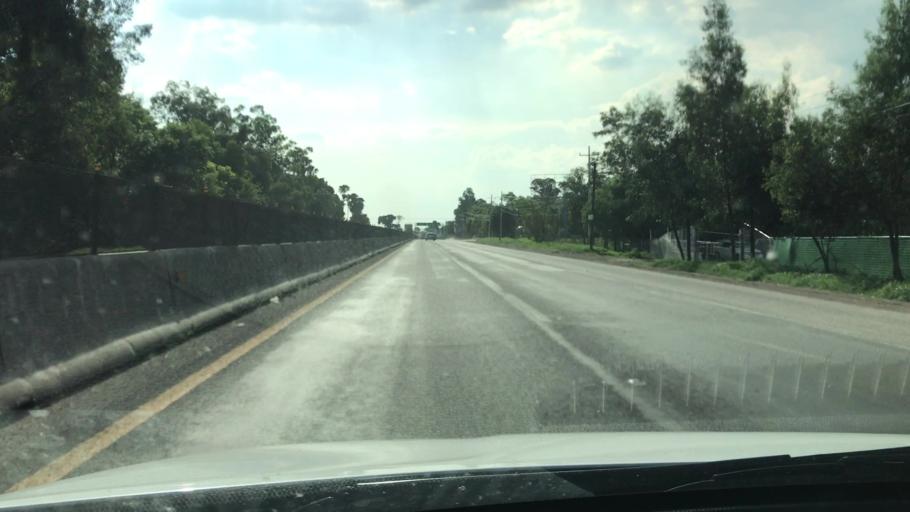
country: MX
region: Guanajuato
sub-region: Salamanca
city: El Divisador
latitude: 20.5552
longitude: -101.1567
